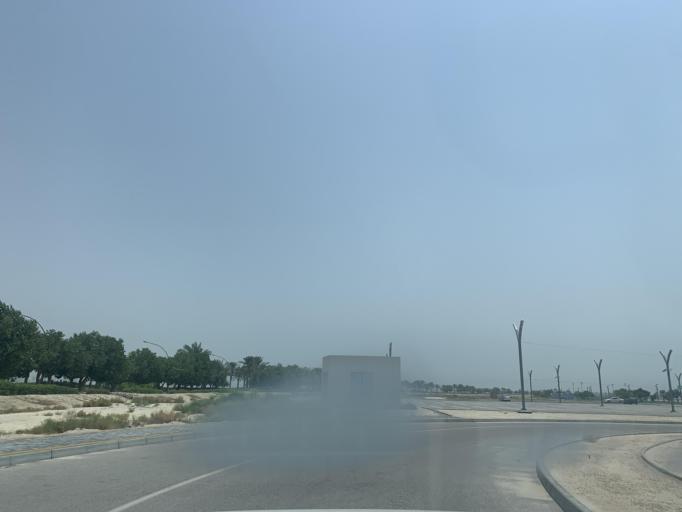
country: BH
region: Central Governorate
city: Dar Kulayb
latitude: 25.8465
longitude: 50.5971
